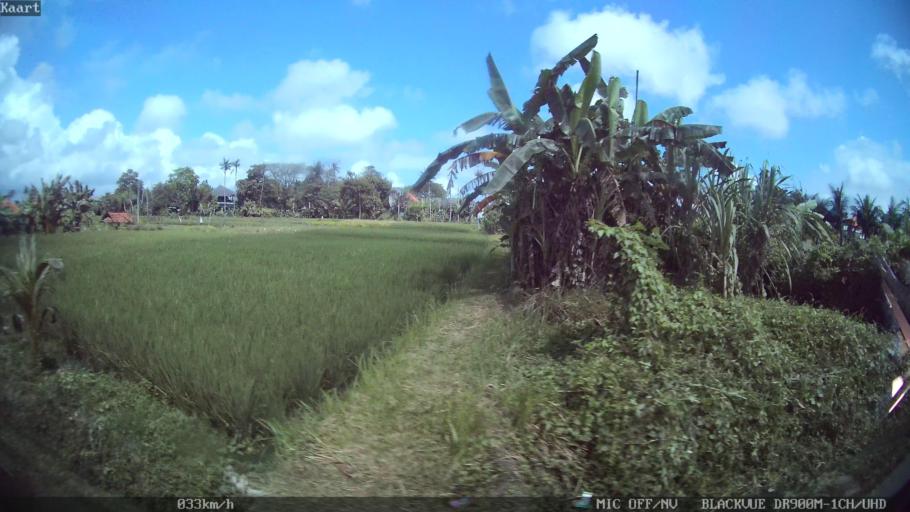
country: ID
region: Bali
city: Banjar Sedang
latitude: -8.5544
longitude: 115.2753
